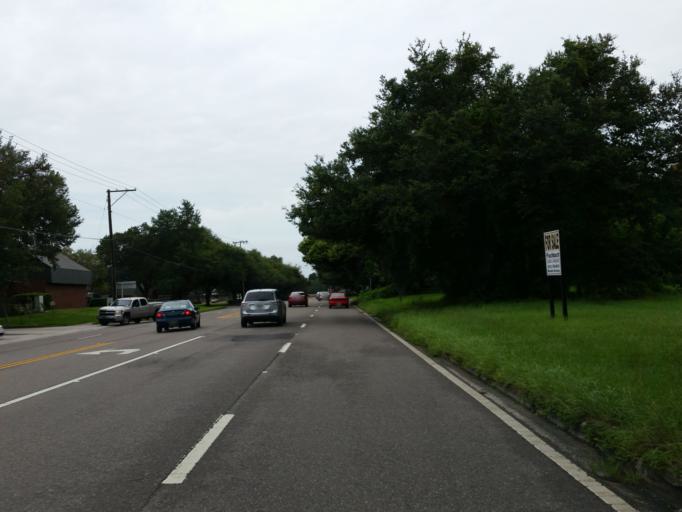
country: US
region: Florida
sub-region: Hillsborough County
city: Brandon
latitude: 27.9342
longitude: -82.3035
